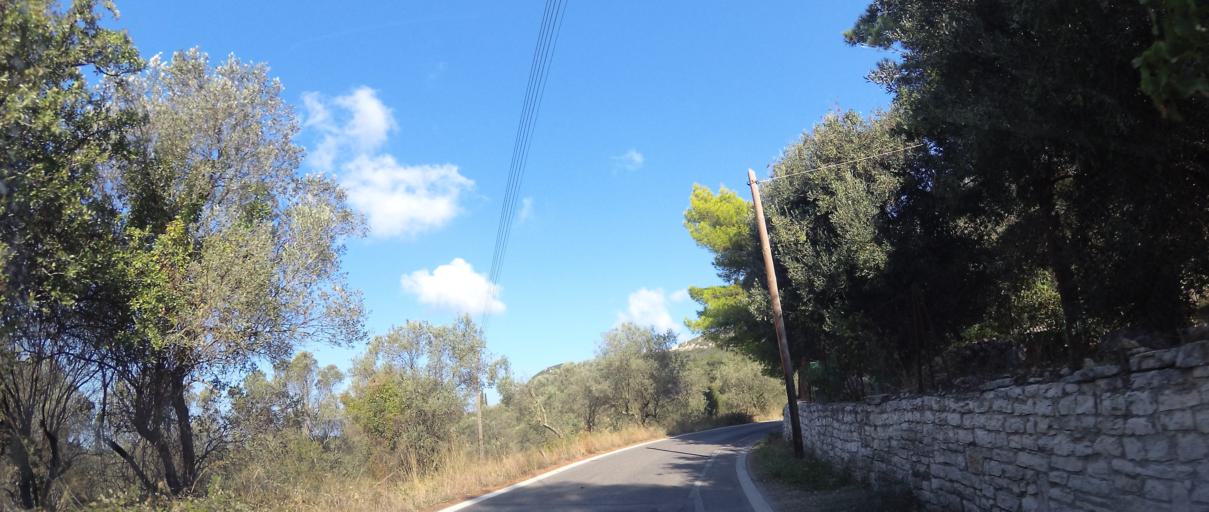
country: GR
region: Ionian Islands
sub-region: Nomos Kerkyras
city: Acharavi
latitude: 39.7222
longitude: 19.8340
